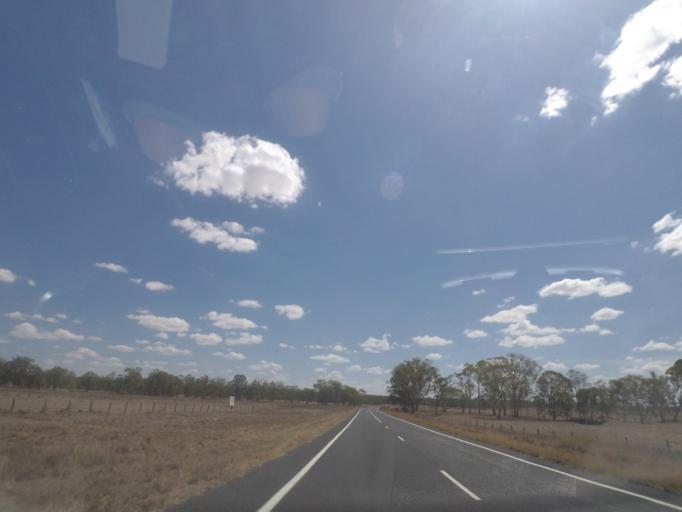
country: AU
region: Queensland
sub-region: Southern Downs
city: Warwick
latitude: -28.1820
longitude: 151.8192
